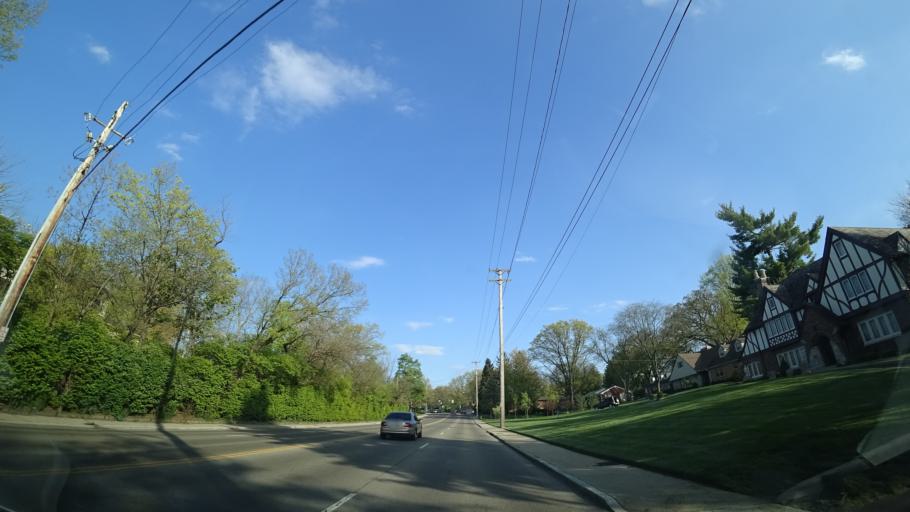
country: US
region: Ohio
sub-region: Montgomery County
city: Oakwood
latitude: 39.7290
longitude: -84.1804
